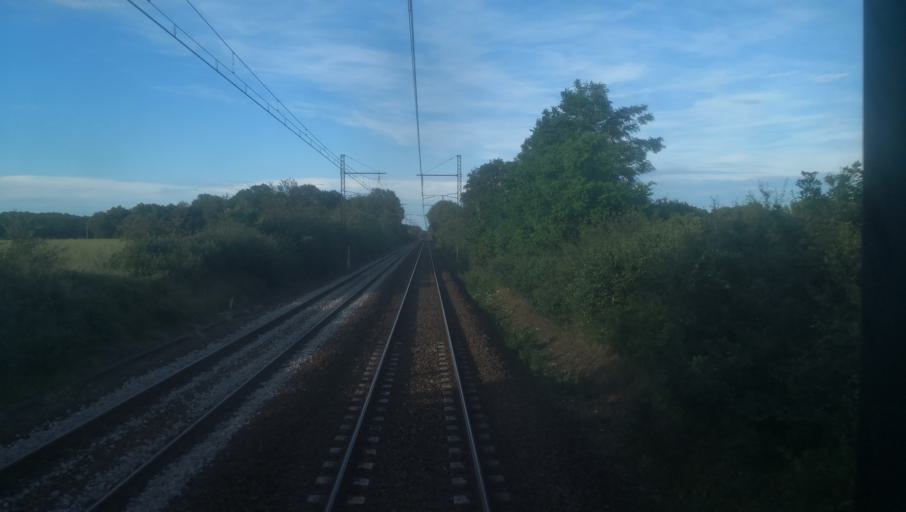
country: FR
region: Centre
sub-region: Departement de l'Indre
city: Deols
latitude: 46.8279
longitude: 1.7436
